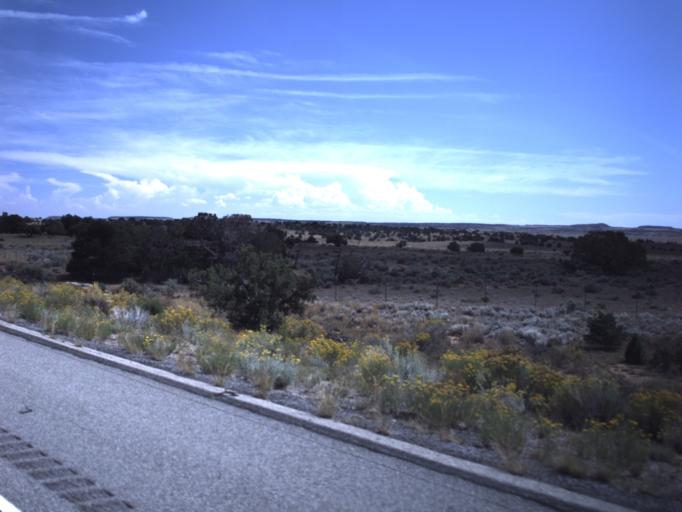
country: US
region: Utah
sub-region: Emery County
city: Castle Dale
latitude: 38.8690
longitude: -110.7216
